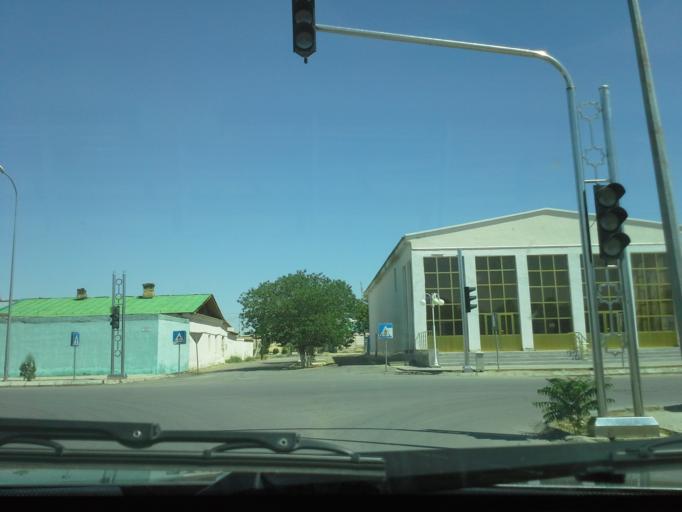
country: TM
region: Balkan
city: Serdar
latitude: 38.9752
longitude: 56.2731
